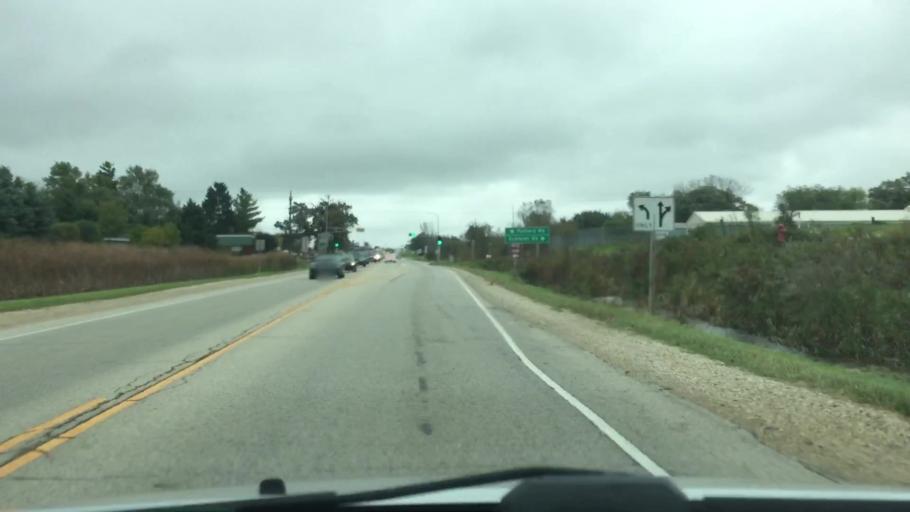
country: US
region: Wisconsin
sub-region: Walworth County
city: Elkhorn
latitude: 42.7077
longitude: -88.5421
